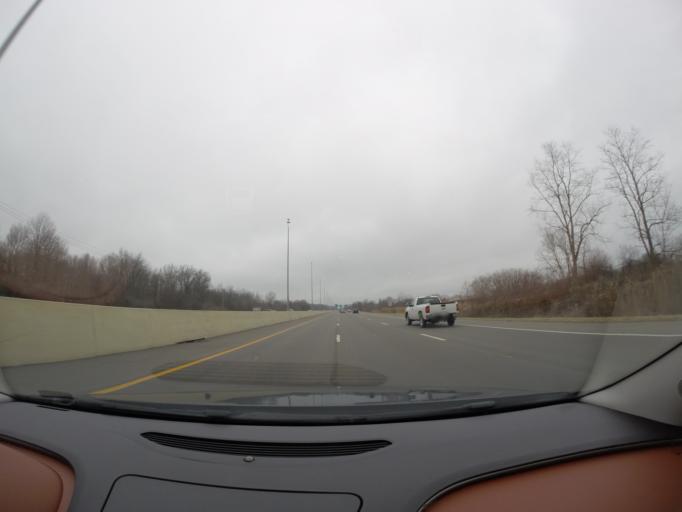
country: US
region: Ohio
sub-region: Summit County
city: Fairlawn
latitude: 41.1192
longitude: -81.6302
